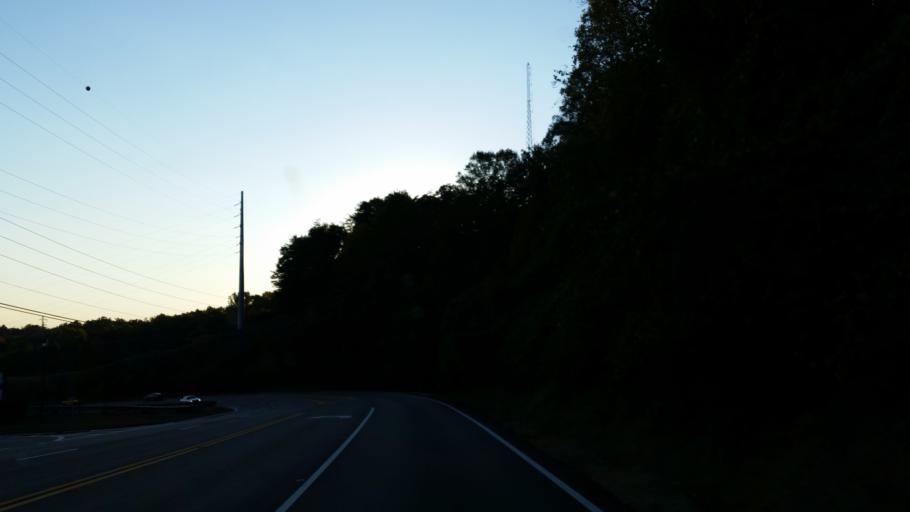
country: US
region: Georgia
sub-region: Lumpkin County
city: Dahlonega
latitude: 34.5222
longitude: -83.9753
